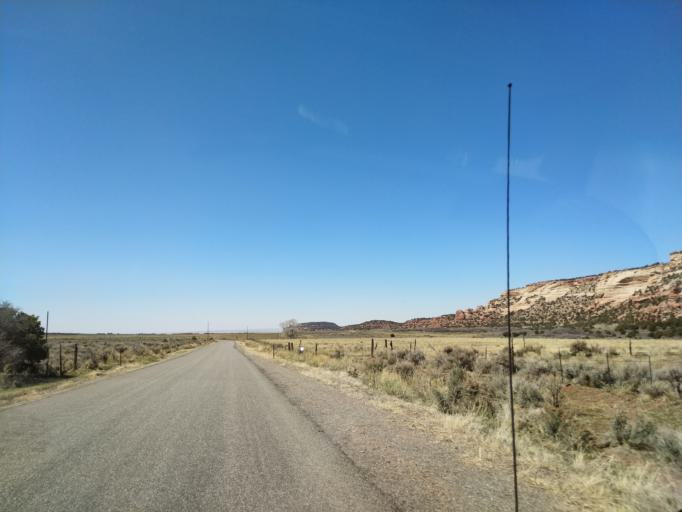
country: US
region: Colorado
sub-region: Mesa County
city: Loma
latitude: 38.9547
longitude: -109.0262
